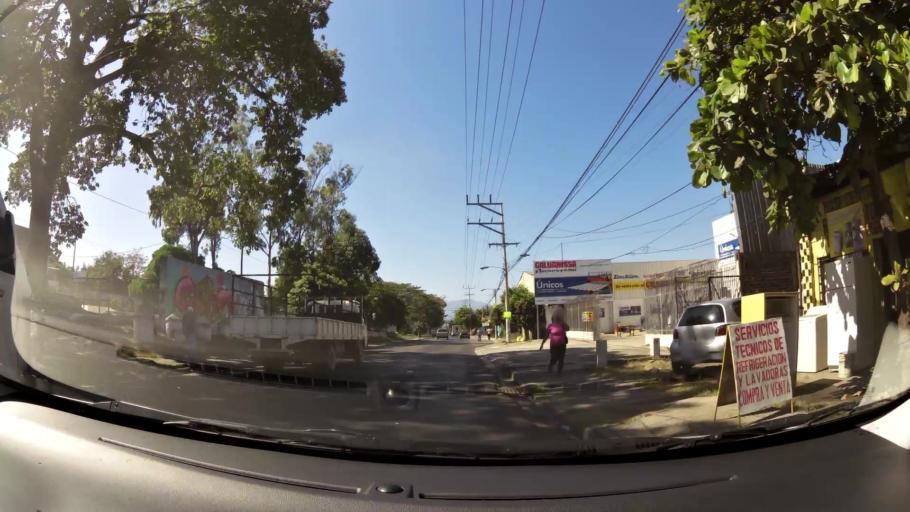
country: SV
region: La Libertad
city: Santa Tecla
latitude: 13.7247
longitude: -89.3712
